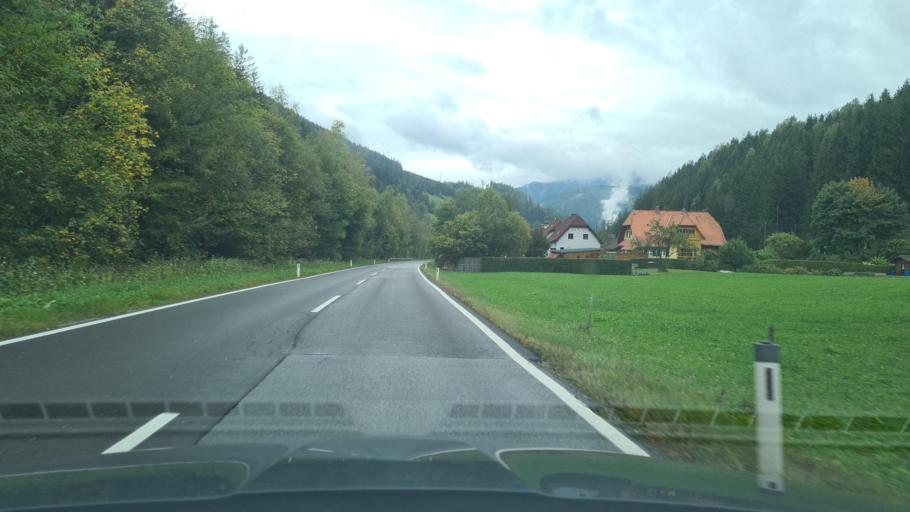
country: AT
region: Styria
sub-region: Politischer Bezirk Weiz
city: Gasen
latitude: 47.3849
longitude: 15.4670
